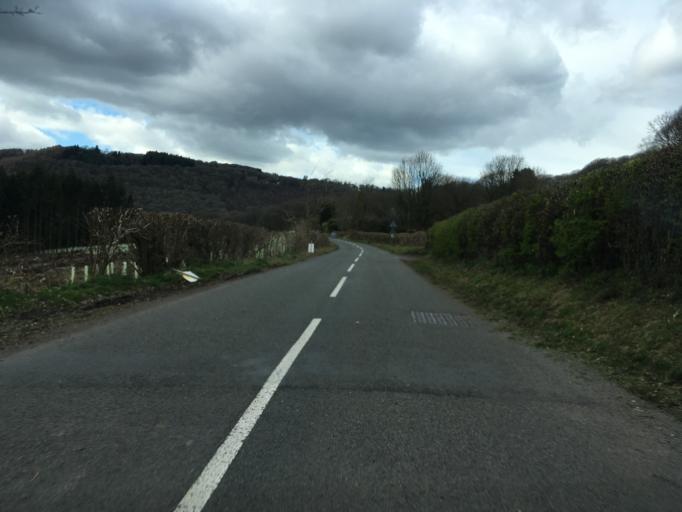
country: GB
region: Wales
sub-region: Monmouthshire
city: Tintern
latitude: 51.7457
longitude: -2.6556
